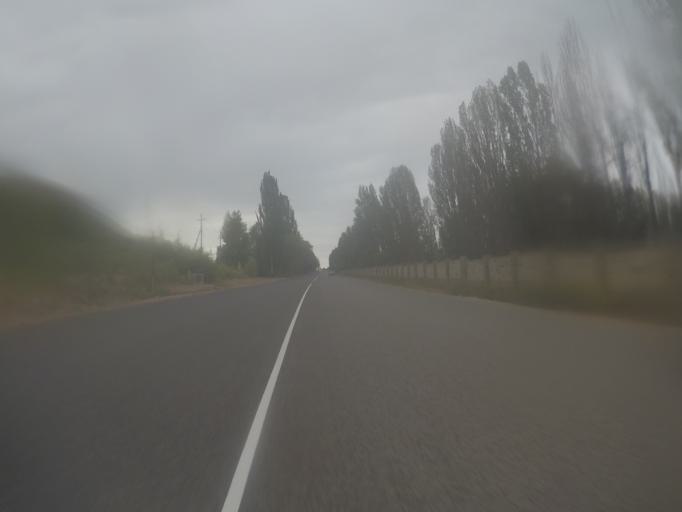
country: KG
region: Ysyk-Koel
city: Cholpon-Ata
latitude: 42.6696
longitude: 77.2760
